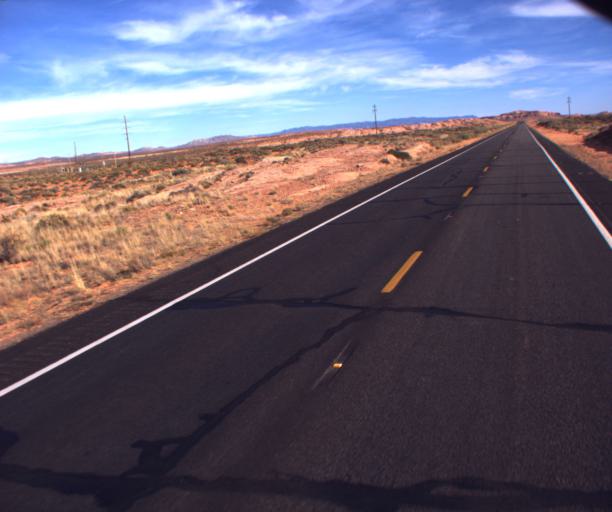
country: US
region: Arizona
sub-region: Apache County
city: Many Farms
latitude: 36.9387
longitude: -109.6389
